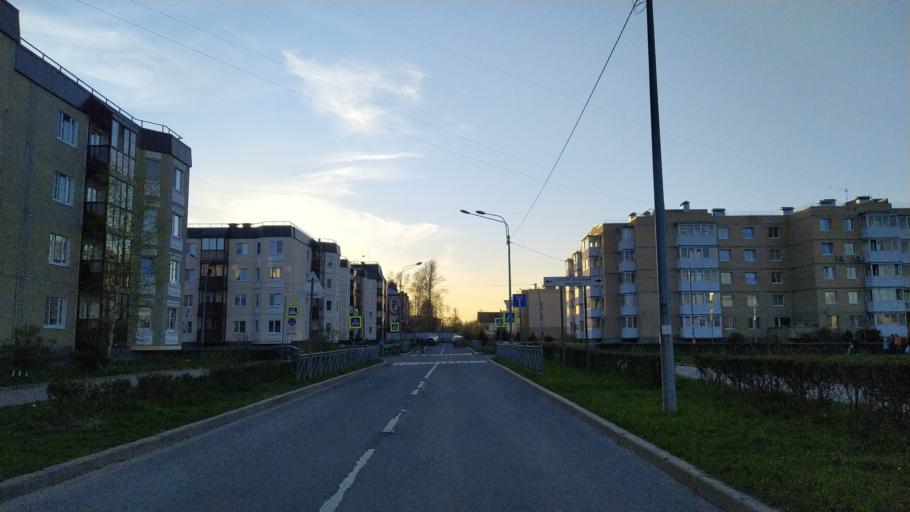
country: RU
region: St.-Petersburg
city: Pushkin
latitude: 59.7046
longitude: 30.3806
